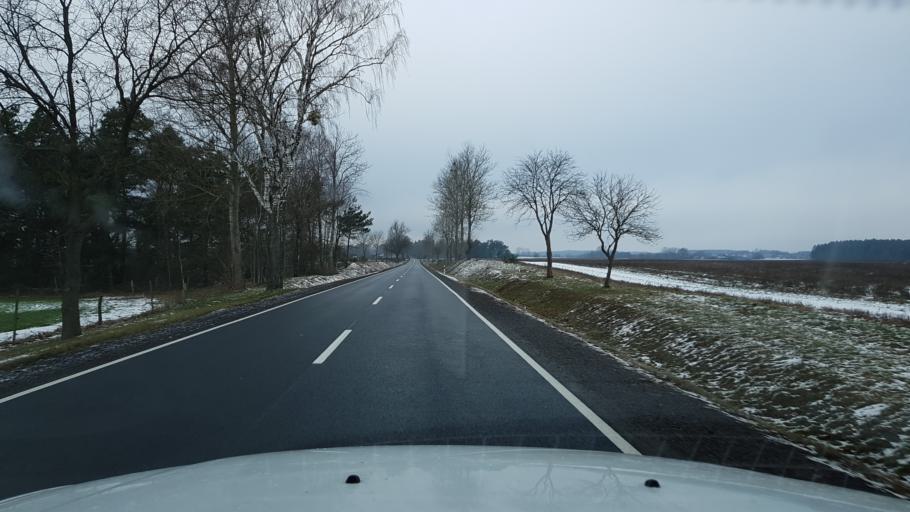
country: PL
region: West Pomeranian Voivodeship
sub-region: Powiat szczecinecki
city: Lubowo
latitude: 53.5889
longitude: 16.3700
